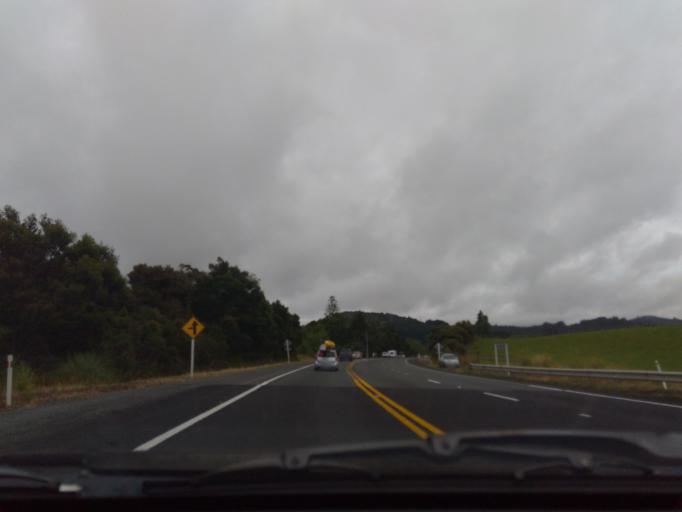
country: NZ
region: Auckland
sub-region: Auckland
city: Wellsford
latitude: -36.1386
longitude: 174.4309
